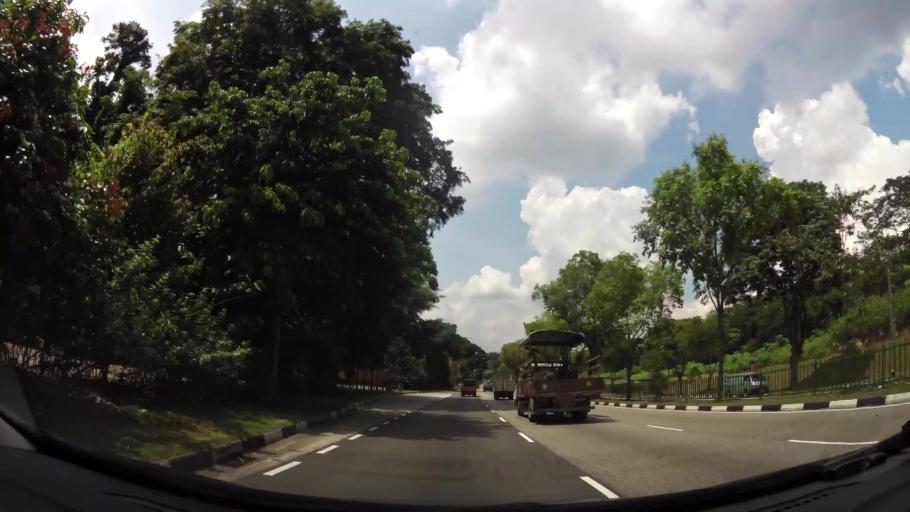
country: MY
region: Johor
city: Johor Bahru
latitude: 1.4106
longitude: 103.7799
